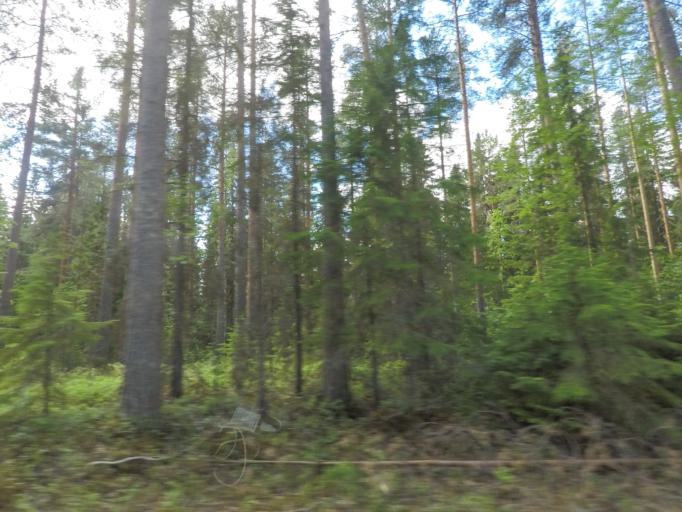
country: FI
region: Central Finland
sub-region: Jyvaeskylae
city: Hankasalmi
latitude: 62.4122
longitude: 26.6438
